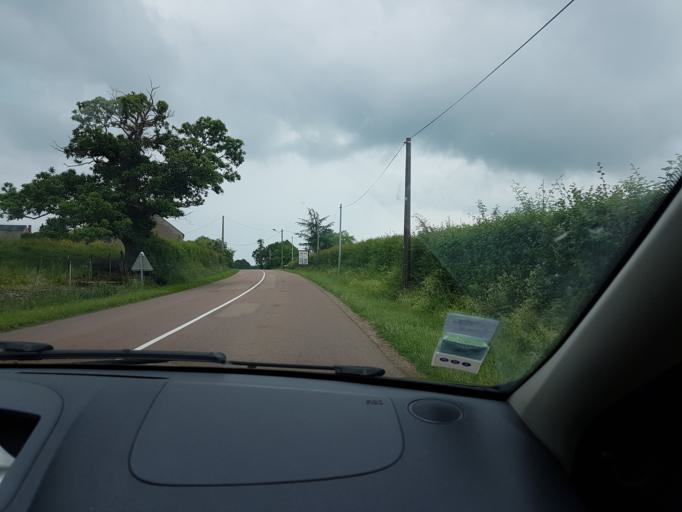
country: FR
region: Bourgogne
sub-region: Departement de la Nievre
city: Corbigny
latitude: 47.2885
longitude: 3.6701
